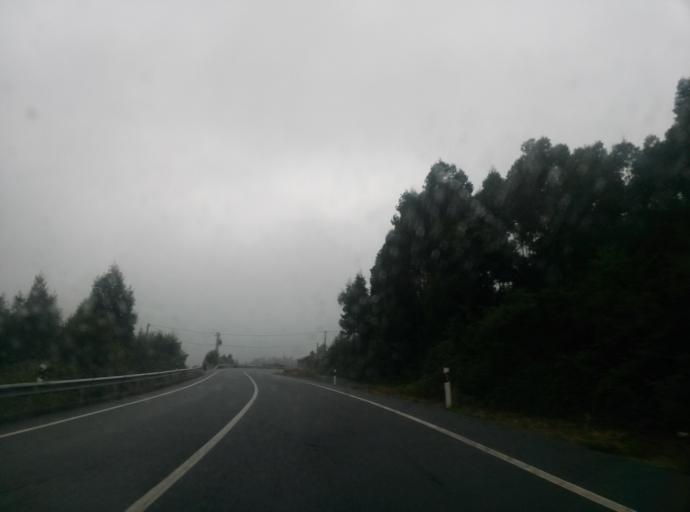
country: ES
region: Galicia
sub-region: Provincia de Lugo
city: Muras
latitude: 43.5502
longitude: -7.6505
